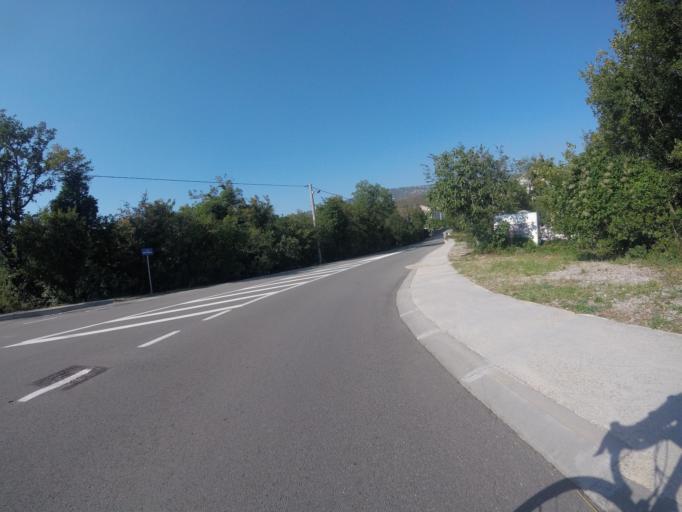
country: HR
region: Primorsko-Goranska
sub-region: Grad Crikvenica
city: Jadranovo
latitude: 45.2285
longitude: 14.6161
